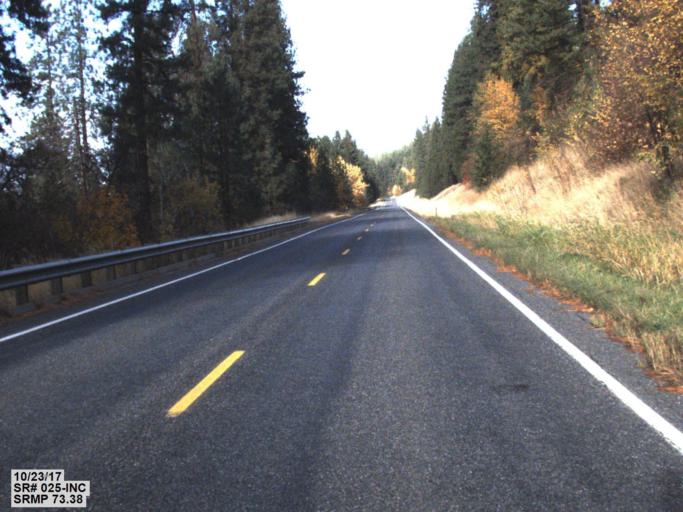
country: US
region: Washington
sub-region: Stevens County
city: Kettle Falls
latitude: 48.5186
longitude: -118.1419
